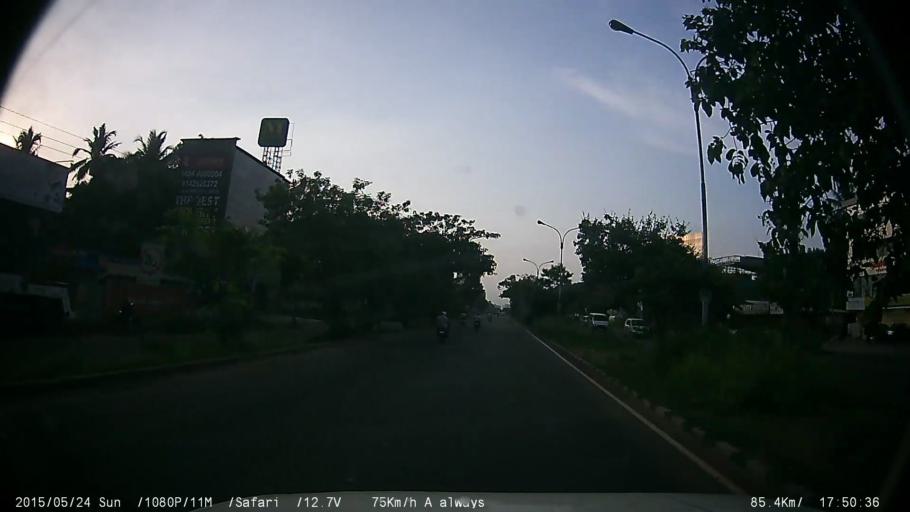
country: IN
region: Kerala
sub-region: Ernakulam
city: Elur
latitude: 10.0000
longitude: 76.3138
